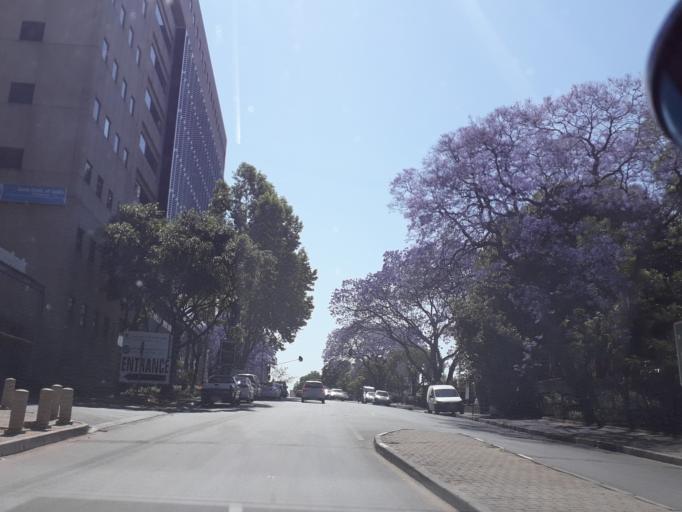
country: ZA
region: Gauteng
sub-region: City of Johannesburg Metropolitan Municipality
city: Johannesburg
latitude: -26.1479
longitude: 28.0415
